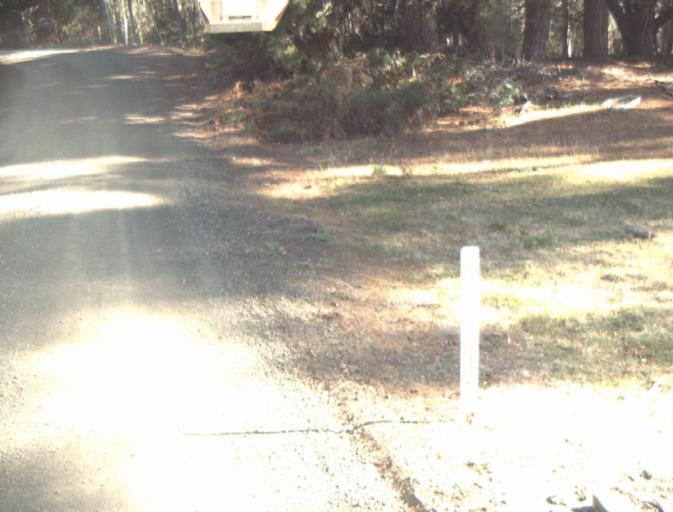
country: AU
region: Tasmania
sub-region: Launceston
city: Mayfield
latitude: -41.2954
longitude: 147.1988
